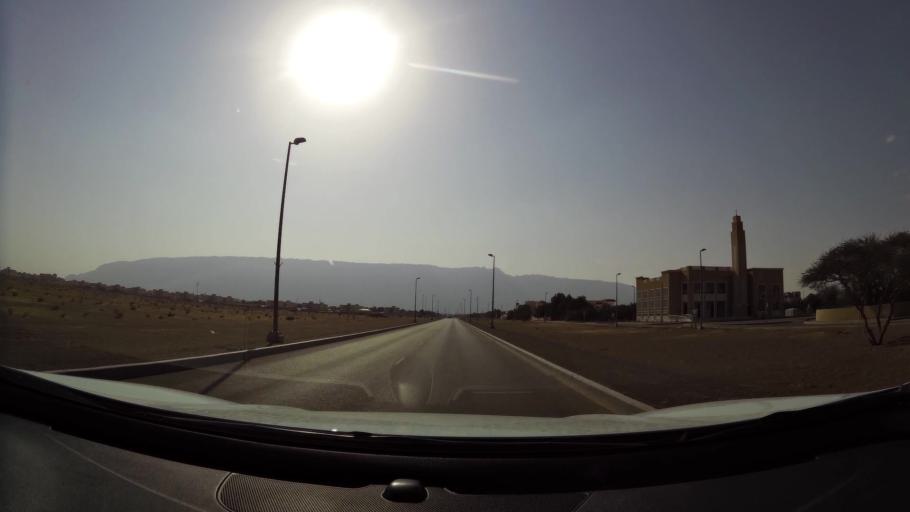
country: AE
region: Abu Dhabi
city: Al Ain
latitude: 24.0679
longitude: 55.8553
